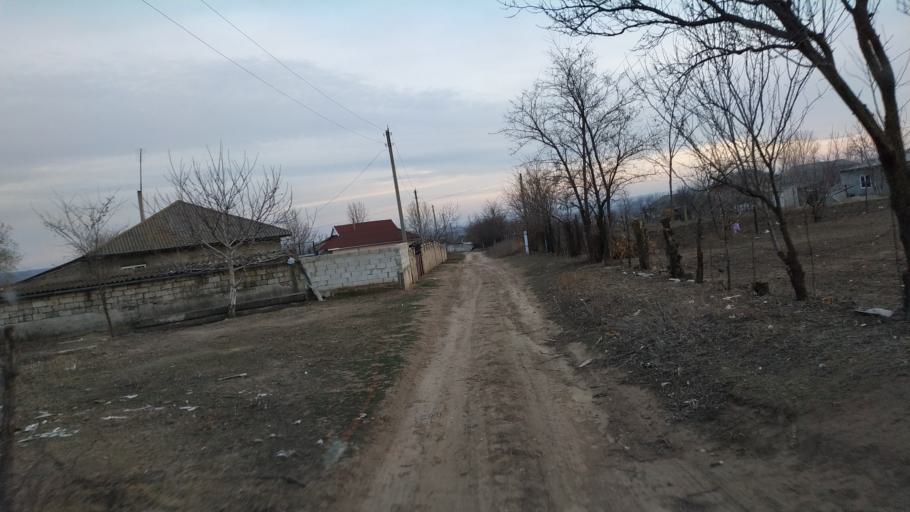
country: MD
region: Hincesti
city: Dancu
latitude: 46.7490
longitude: 28.2106
